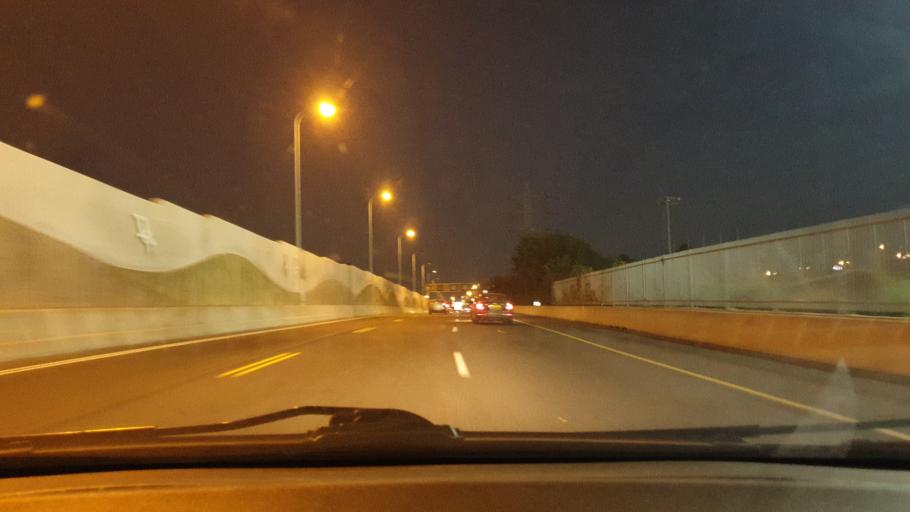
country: IL
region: Tel Aviv
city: Yafo
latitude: 32.0380
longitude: 34.7646
